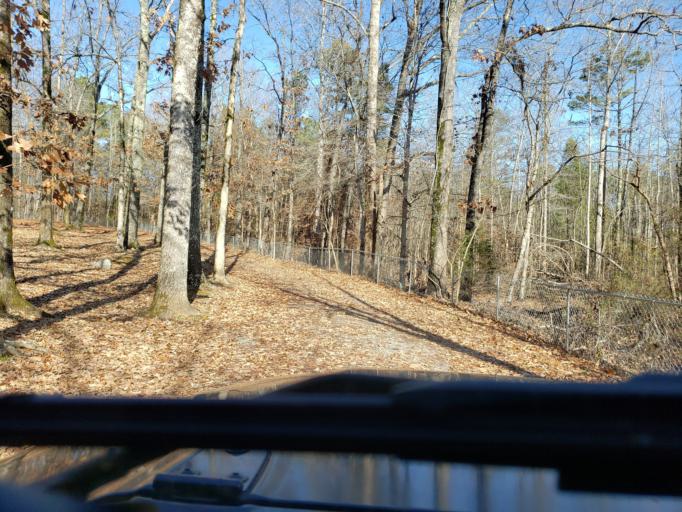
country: US
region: North Carolina
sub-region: Cleveland County
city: White Plains
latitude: 35.1675
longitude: -81.4340
